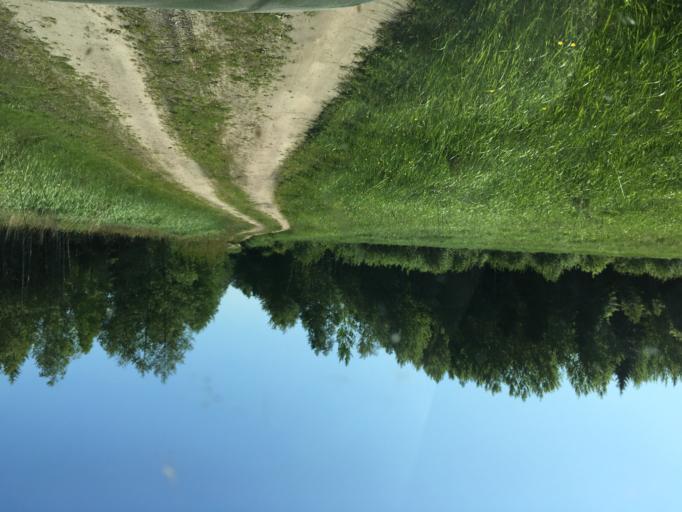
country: LV
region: Ventspils
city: Ventspils
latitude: 57.4800
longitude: 21.7630
